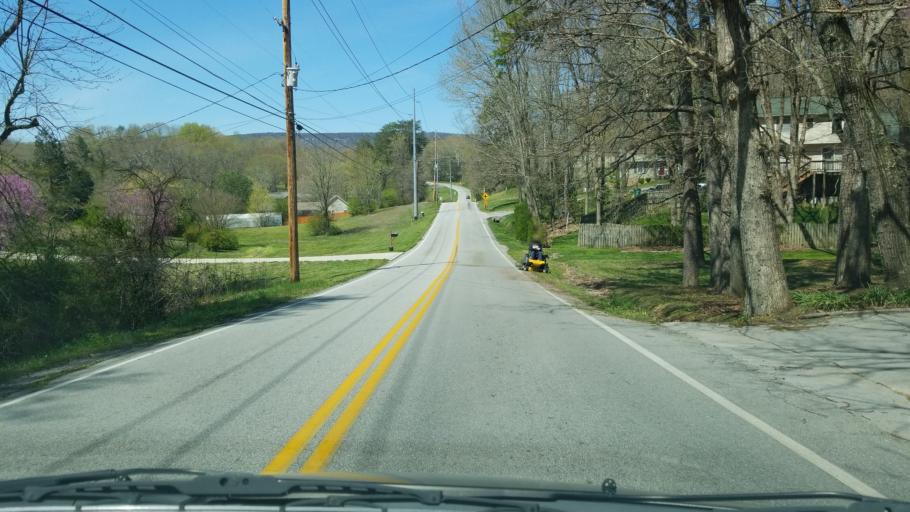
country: US
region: Tennessee
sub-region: Hamilton County
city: Middle Valley
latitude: 35.2010
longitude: -85.2053
